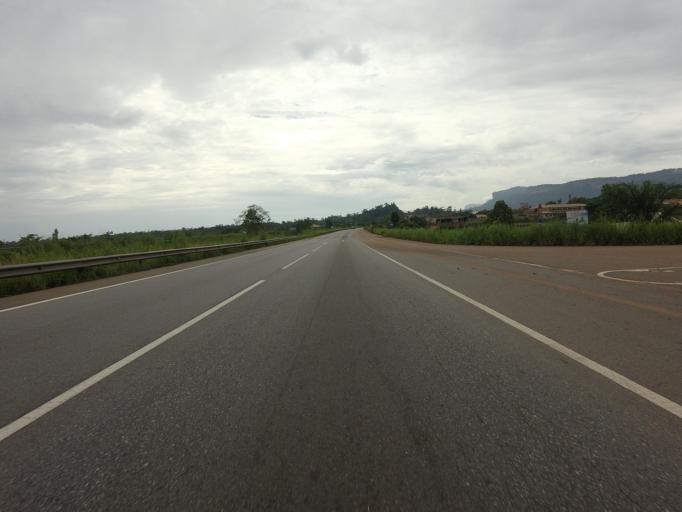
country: GH
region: Eastern
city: Nkawkaw
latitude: 6.5440
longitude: -0.7901
